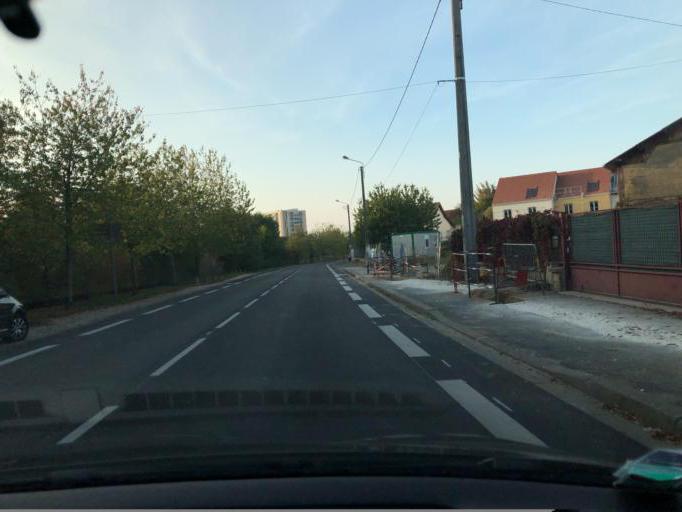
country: FR
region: Bourgogne
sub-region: Departement de l'Yonne
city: Sens
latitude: 48.2021
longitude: 3.2984
